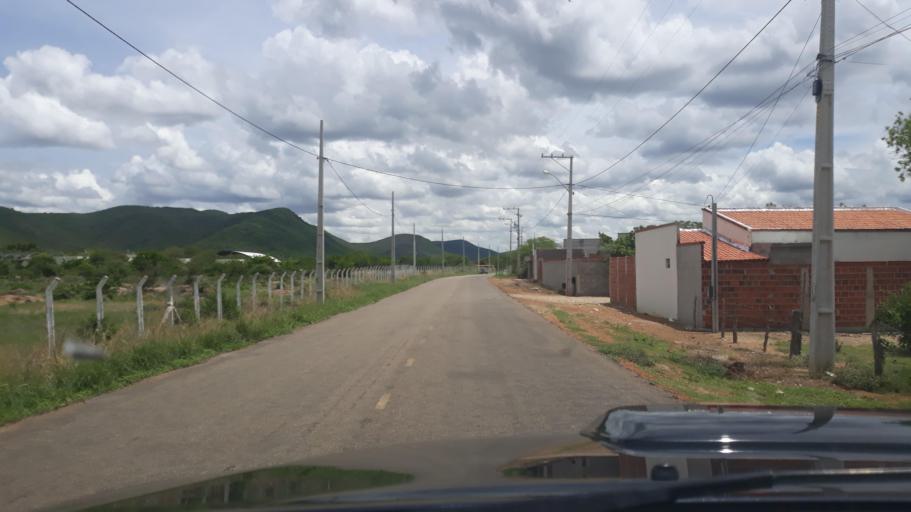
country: BR
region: Bahia
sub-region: Guanambi
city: Guanambi
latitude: -14.2993
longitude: -42.6958
